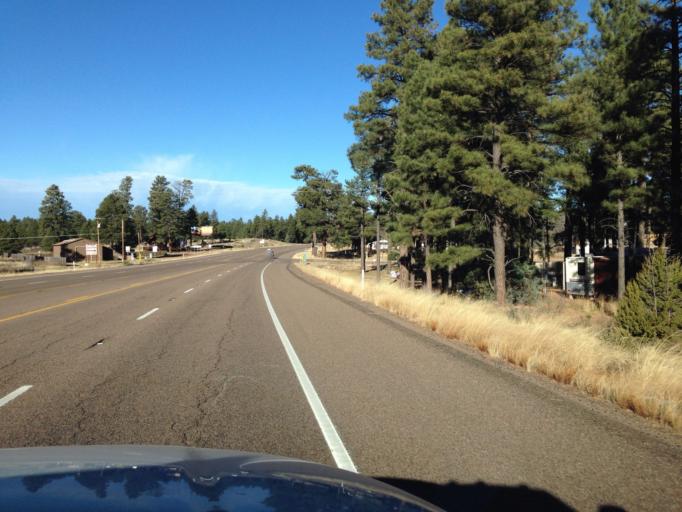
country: US
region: Arizona
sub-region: Navajo County
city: Heber-Overgaard
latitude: 34.3901
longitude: -110.5512
